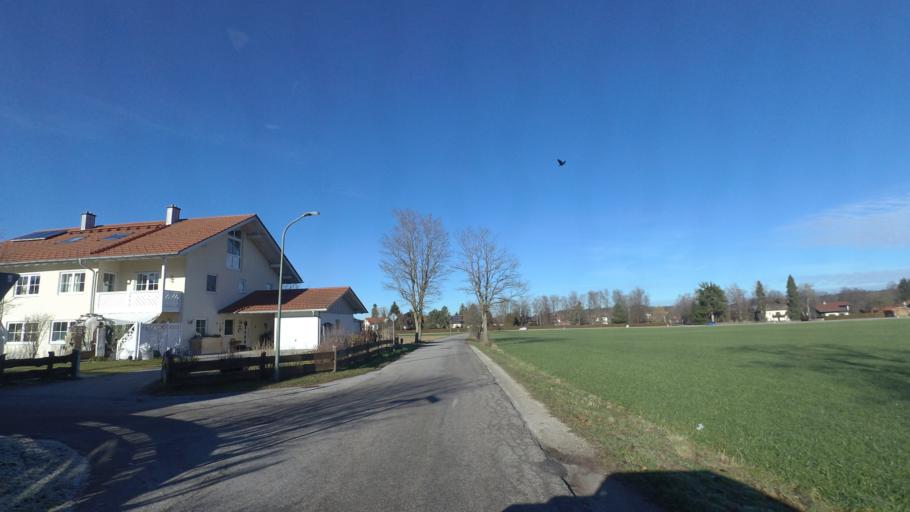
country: DE
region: Bavaria
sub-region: Upper Bavaria
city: Grabenstatt
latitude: 47.8396
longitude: 12.5461
